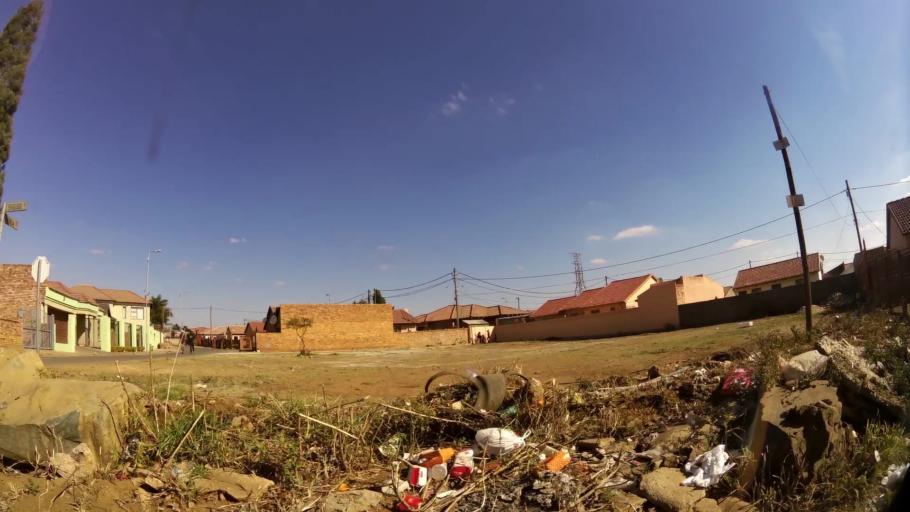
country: ZA
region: Gauteng
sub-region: City of Tshwane Metropolitan Municipality
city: Cullinan
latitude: -25.7154
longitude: 28.3994
